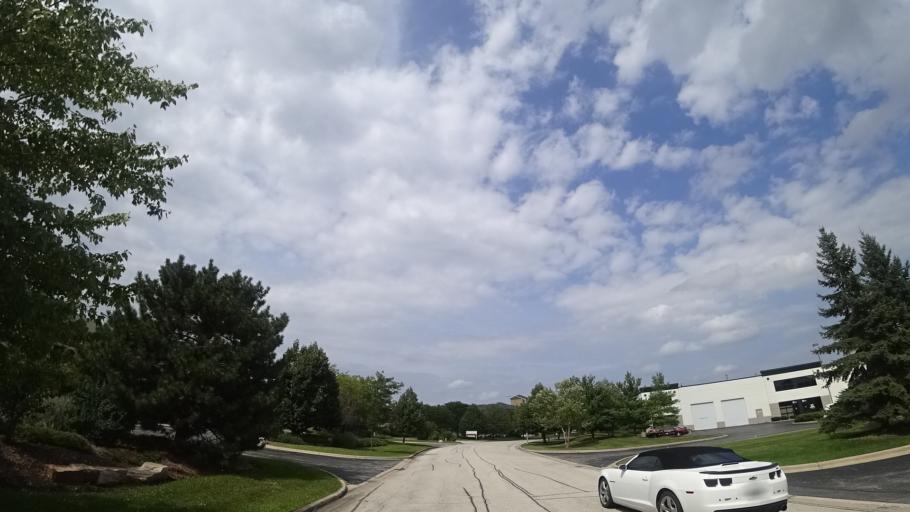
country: US
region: Illinois
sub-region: Cook County
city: Tinley Park
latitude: 41.5548
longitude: -87.7980
